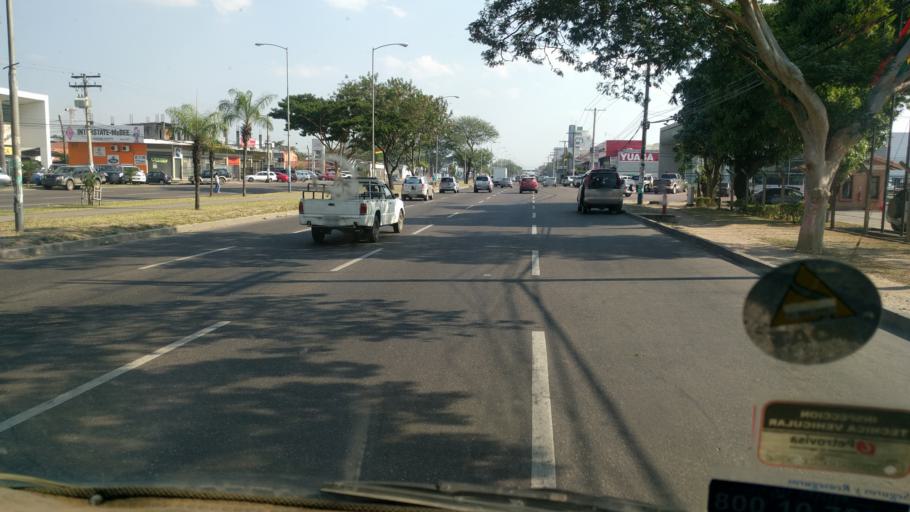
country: BO
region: Santa Cruz
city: Santa Cruz de la Sierra
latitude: -17.8067
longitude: -63.2026
